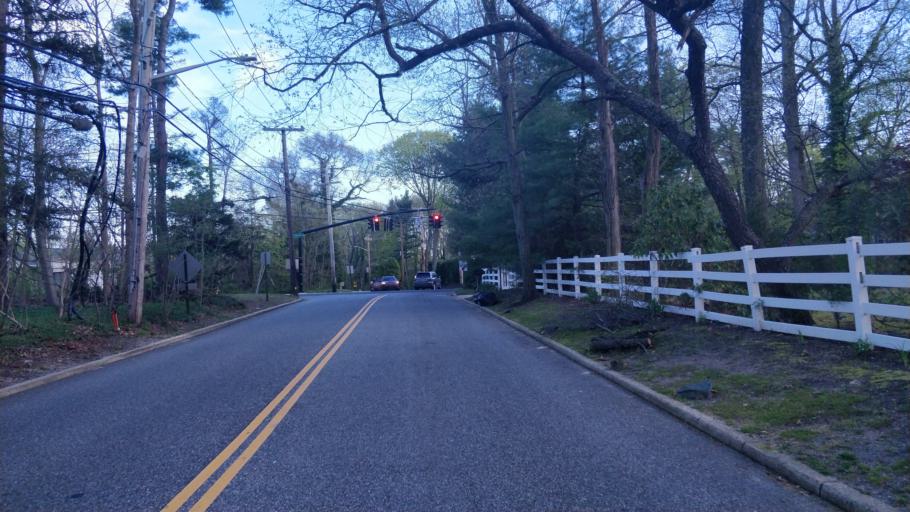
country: US
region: New York
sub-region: Suffolk County
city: Village of the Branch
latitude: 40.8664
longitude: -73.1887
